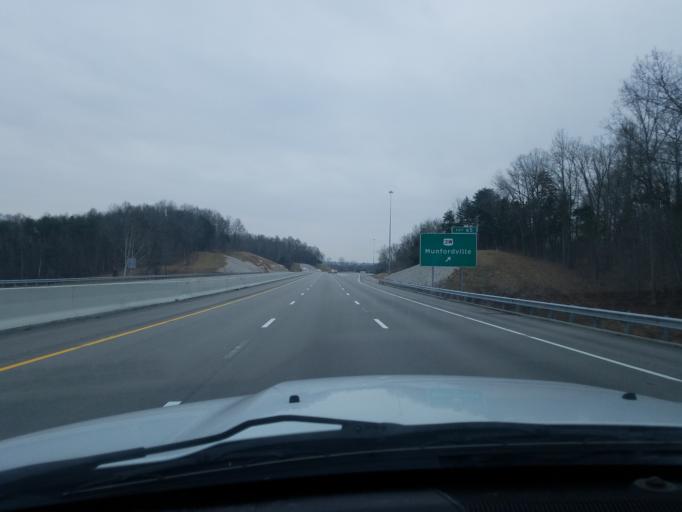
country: US
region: Kentucky
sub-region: Hart County
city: Munfordville
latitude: 37.3010
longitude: -85.9021
